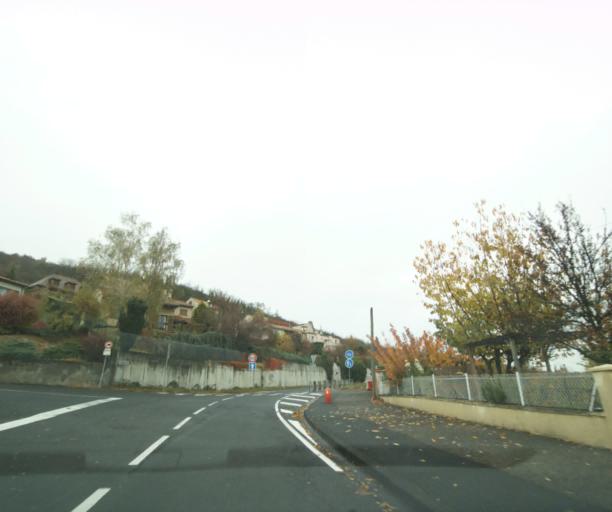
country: FR
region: Auvergne
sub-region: Departement du Puy-de-Dome
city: Cournon-d'Auvergne
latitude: 45.7506
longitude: 3.2044
